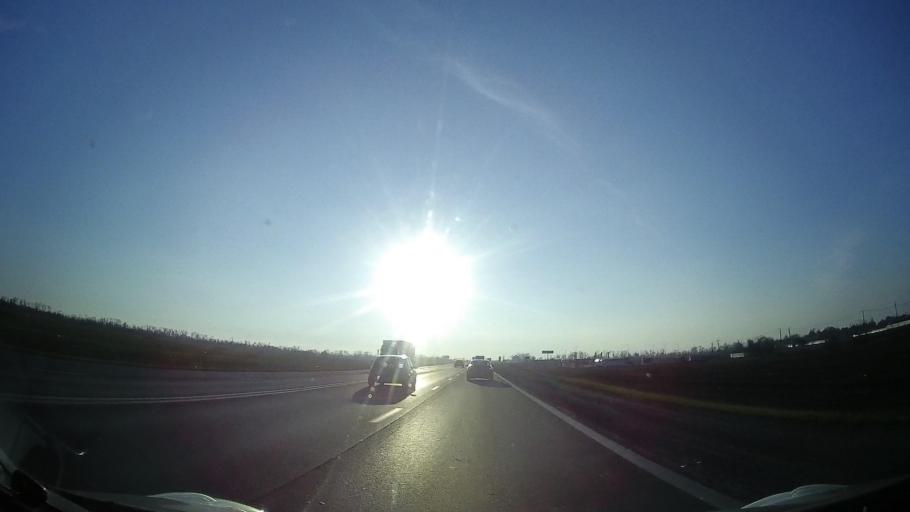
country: RU
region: Rostov
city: Bataysk
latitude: 47.0877
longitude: 39.7883
